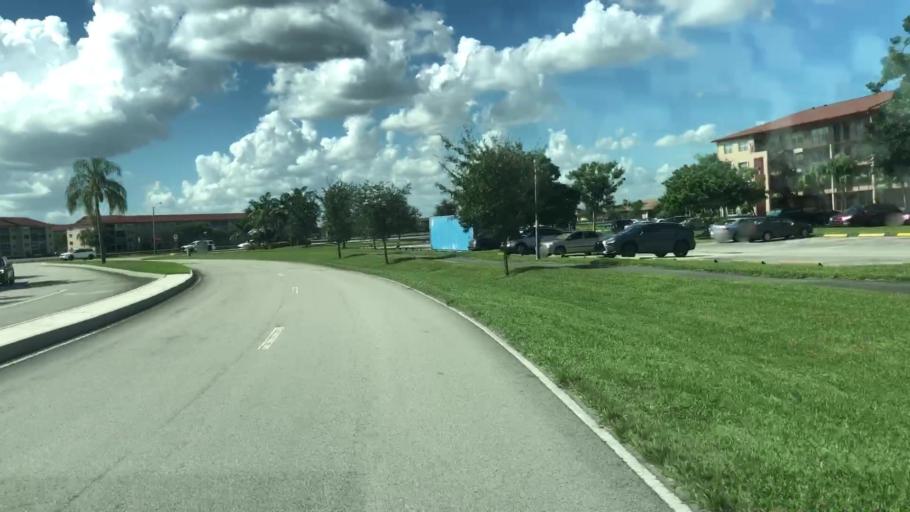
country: US
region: Florida
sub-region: Broward County
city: Sunshine Ranches
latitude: 26.0012
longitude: -80.3220
